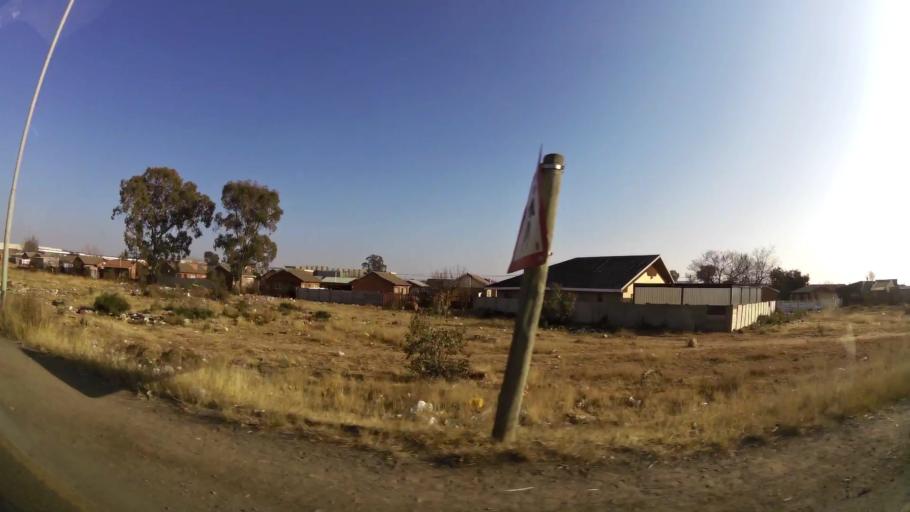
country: ZA
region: Orange Free State
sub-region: Mangaung Metropolitan Municipality
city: Bloemfontein
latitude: -29.1590
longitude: 26.2602
